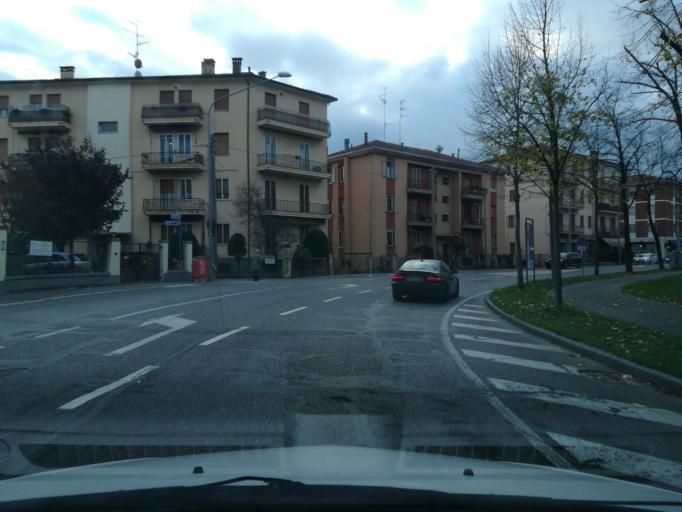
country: IT
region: Emilia-Romagna
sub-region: Provincia di Bologna
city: Imola
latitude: 44.3534
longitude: 11.7208
